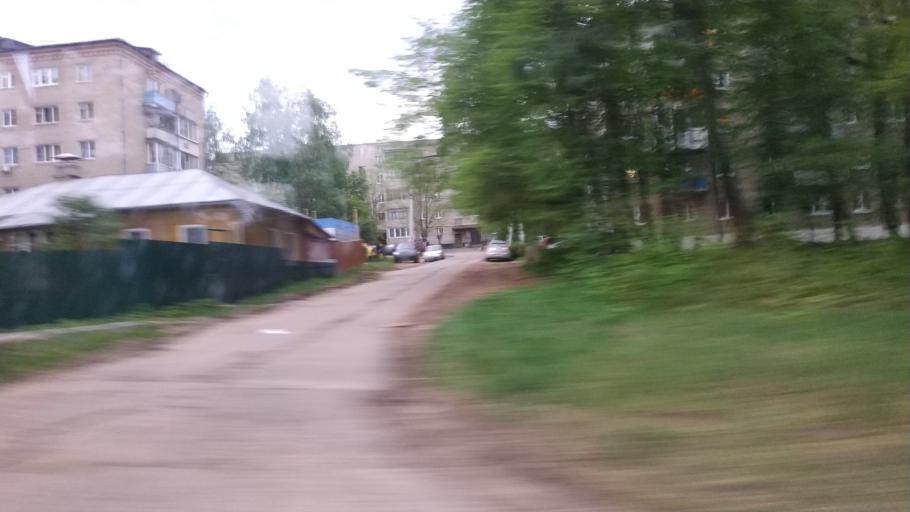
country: RU
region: Moskovskaya
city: Kashira
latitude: 54.8539
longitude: 38.1804
